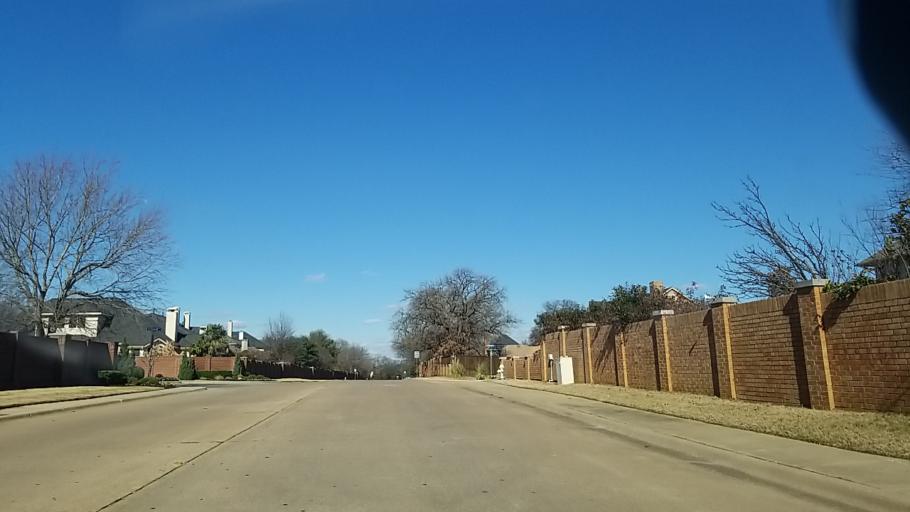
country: US
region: Texas
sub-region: Denton County
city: Corinth
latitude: 33.1607
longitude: -97.0882
